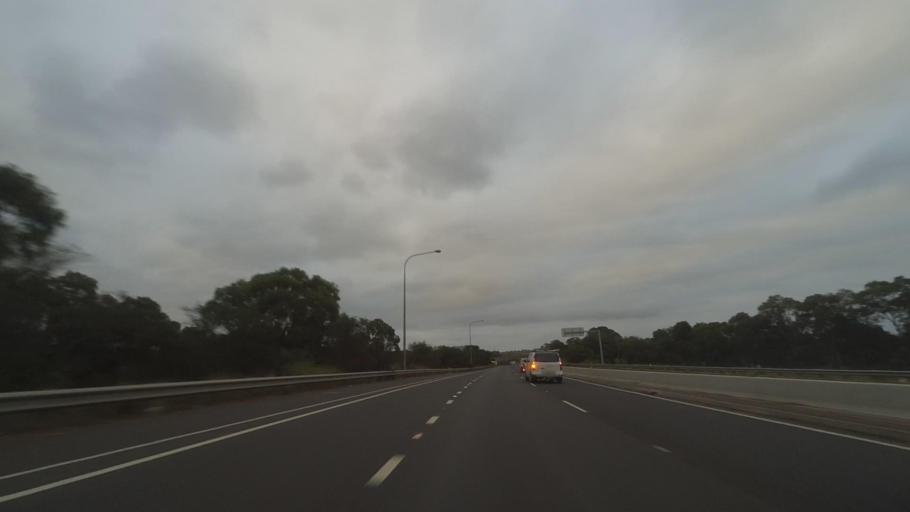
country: AU
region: New South Wales
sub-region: Shellharbour
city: Albion Park Rail
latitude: -34.5390
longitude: 150.7847
